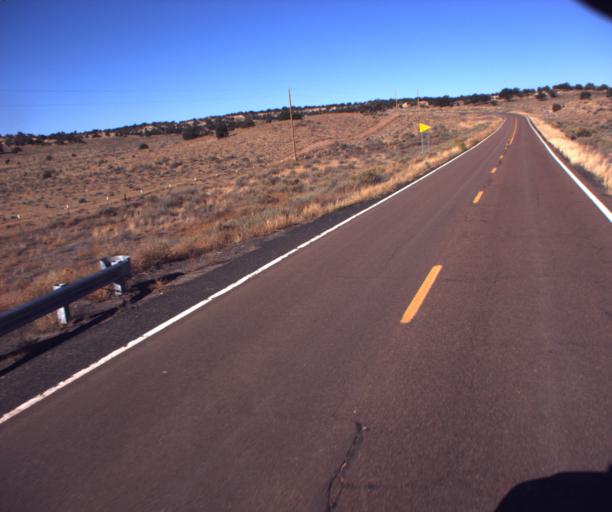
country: US
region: Arizona
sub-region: Navajo County
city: First Mesa
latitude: 35.7657
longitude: -109.9832
